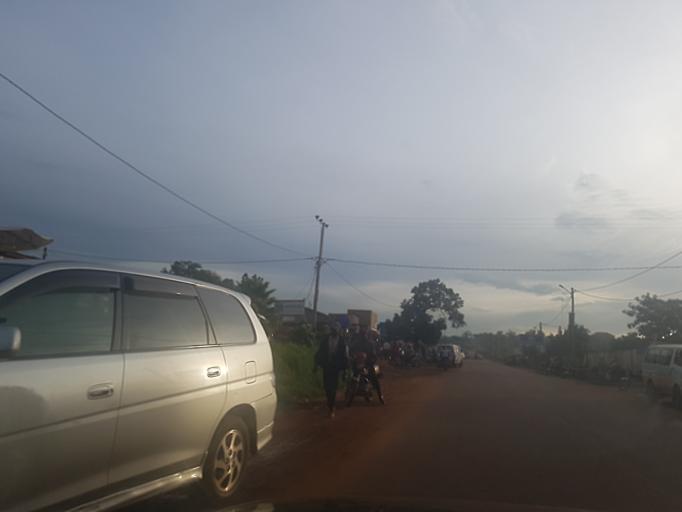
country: UG
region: Central Region
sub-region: Wakiso District
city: Bweyogerere
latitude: 0.3954
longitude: 32.6667
